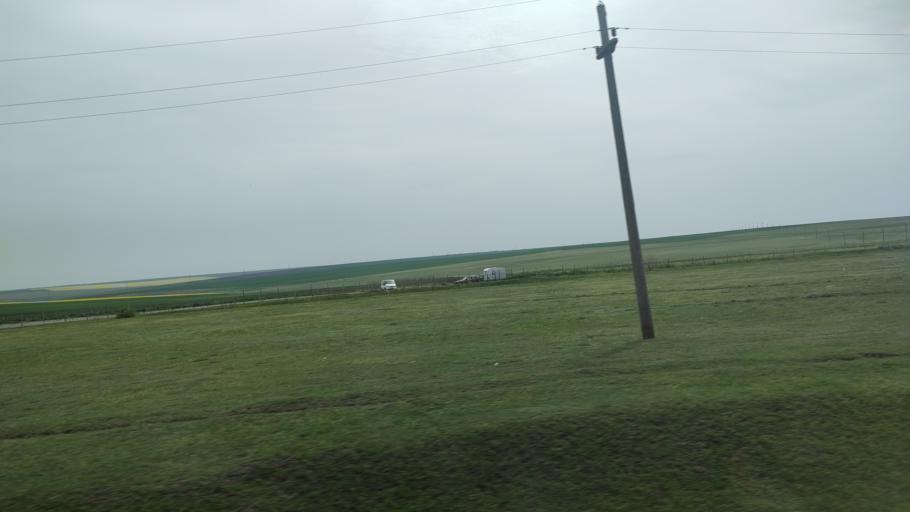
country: RO
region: Constanta
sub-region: Comuna Ciocarlia
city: Ciocarlia de Sus
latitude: 44.1248
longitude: 28.3381
